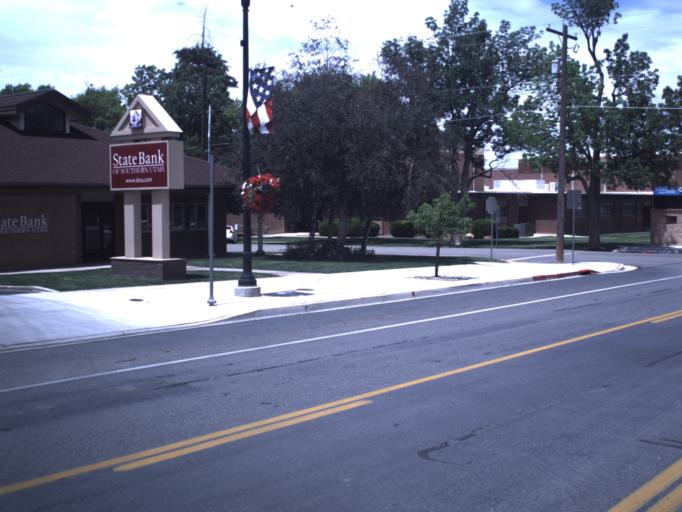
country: US
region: Utah
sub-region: Iron County
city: Parowan
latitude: 37.8439
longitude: -112.8276
